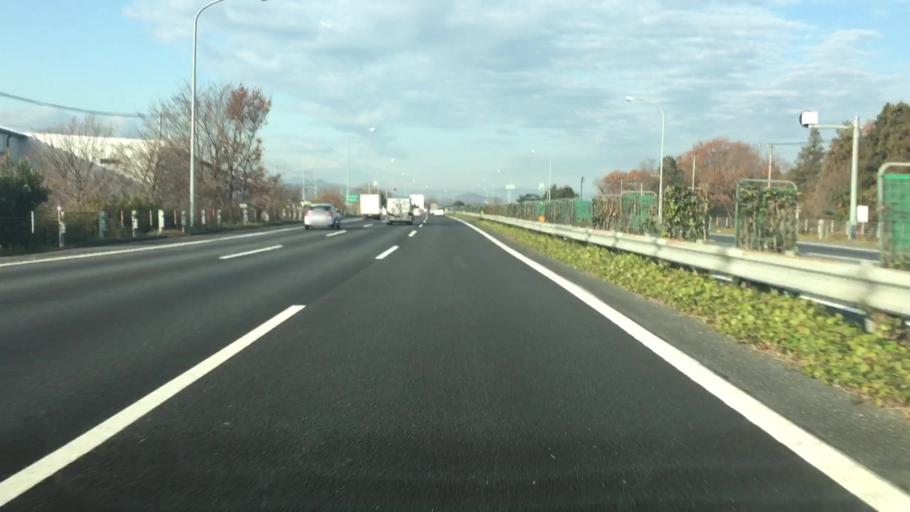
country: JP
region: Saitama
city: Sakado
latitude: 36.0441
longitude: 139.3588
